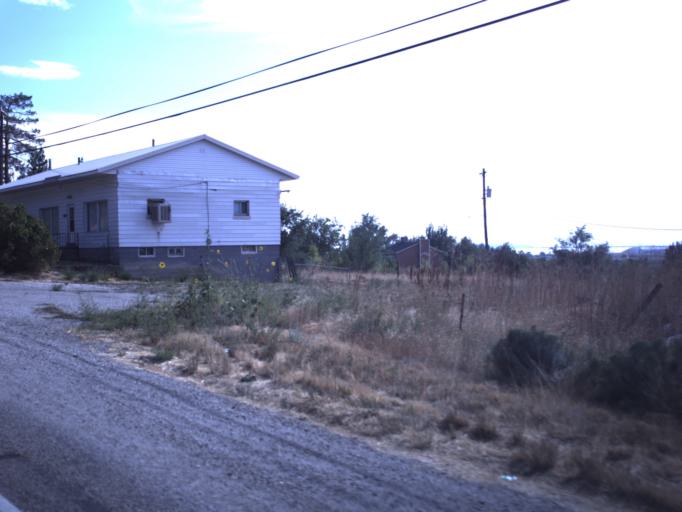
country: US
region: Utah
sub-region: Box Elder County
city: Perry
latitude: 41.4412
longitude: -112.0369
